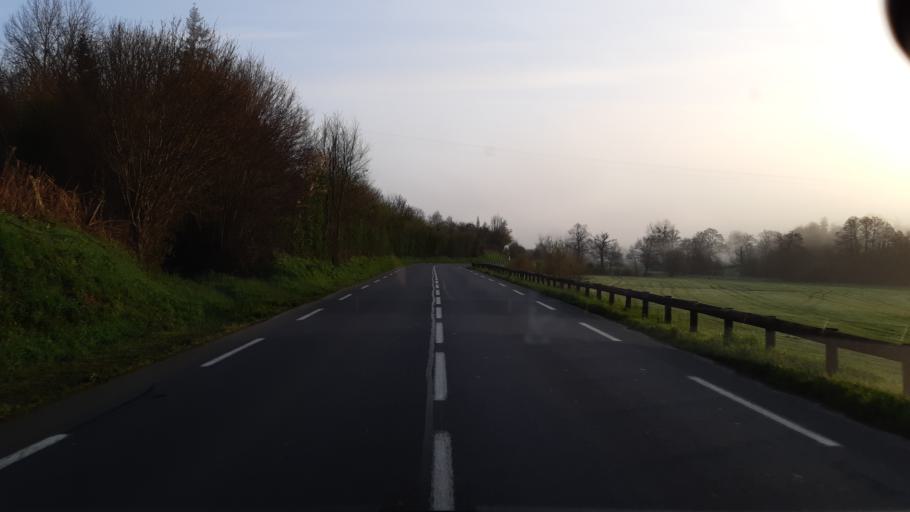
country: FR
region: Lower Normandy
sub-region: Departement de la Manche
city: Agneaux
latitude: 49.0823
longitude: -1.1178
